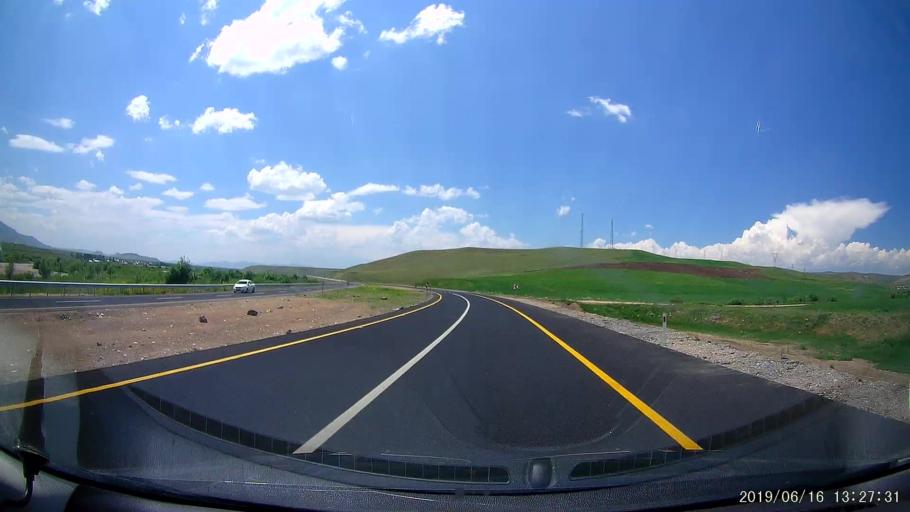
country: TR
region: Agri
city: Murat
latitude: 39.6714
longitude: 43.3089
